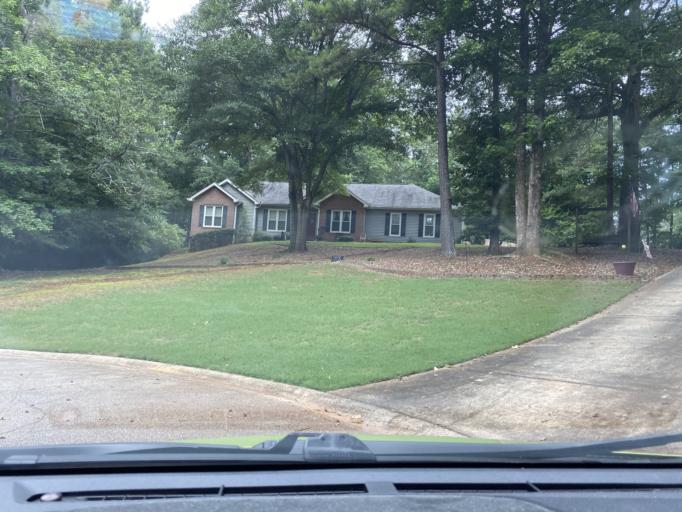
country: US
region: Georgia
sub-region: Fayette County
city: Peachtree City
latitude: 33.4273
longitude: -84.6812
